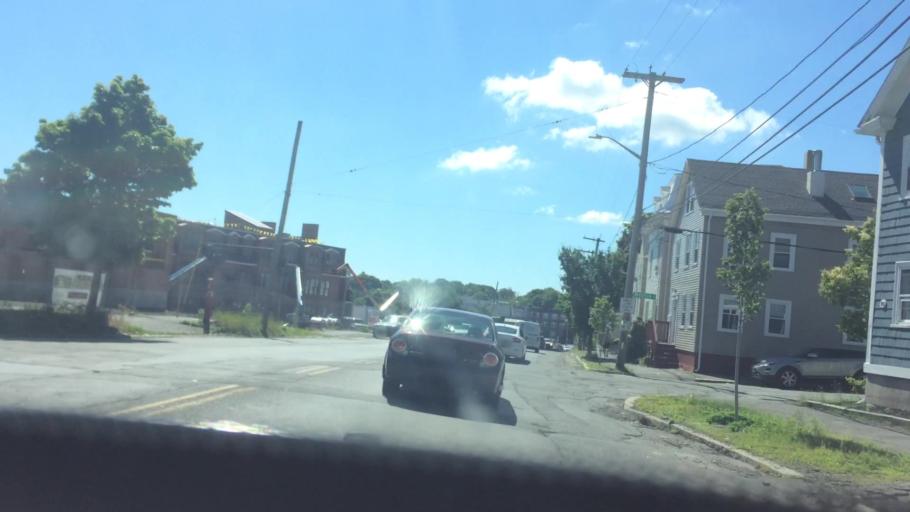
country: US
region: Massachusetts
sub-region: Essex County
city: Salem
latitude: 42.5203
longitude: -70.9115
